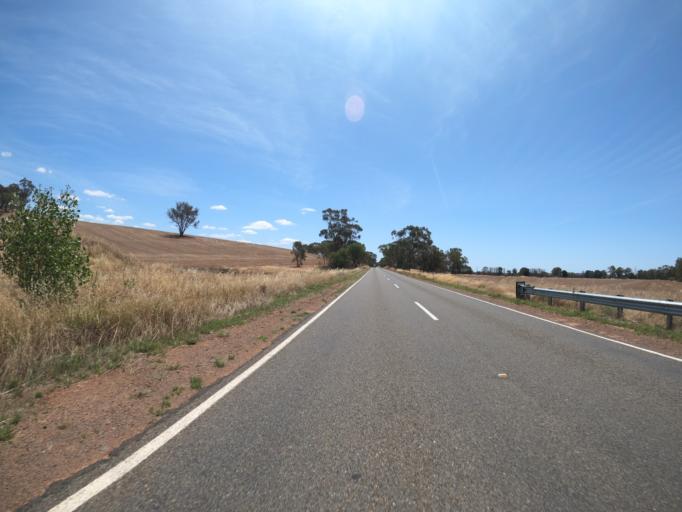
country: AU
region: Victoria
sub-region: Benalla
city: Benalla
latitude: -36.3277
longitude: 145.9608
